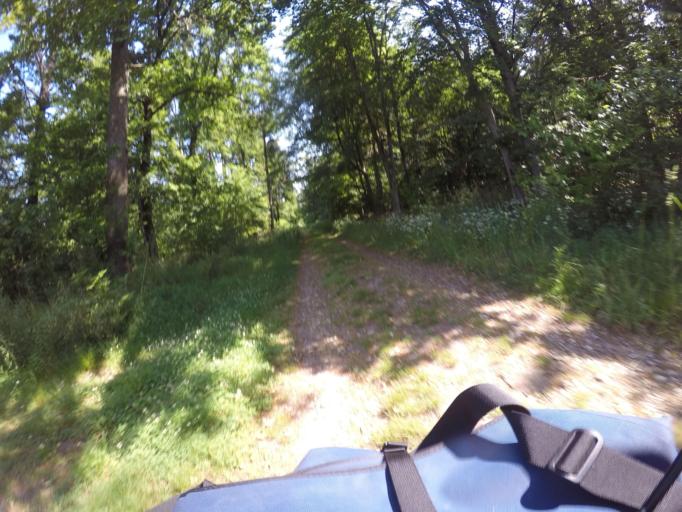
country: DE
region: Baden-Wuerttemberg
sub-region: Karlsruhe Region
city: Rheinstetten
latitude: 48.9440
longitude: 8.3154
